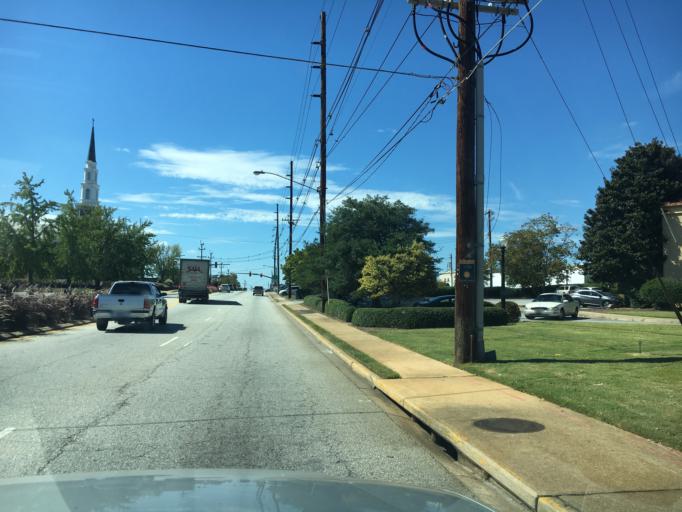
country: US
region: South Carolina
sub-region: Spartanburg County
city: Spartanburg
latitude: 34.9473
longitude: -81.9285
